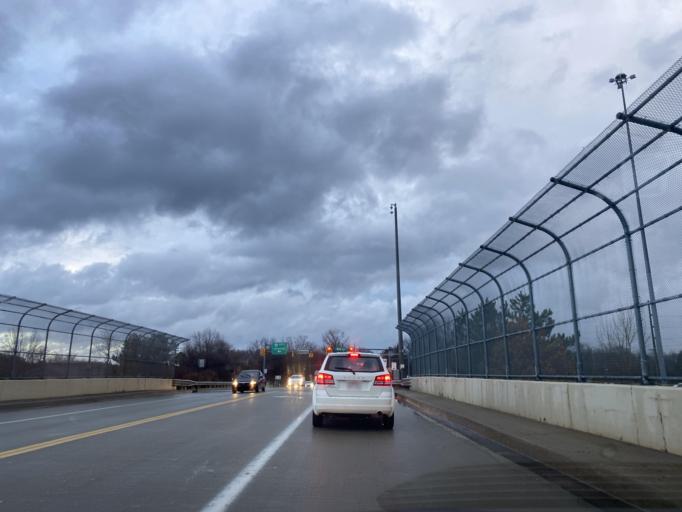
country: IN
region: Maharashtra
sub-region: Pune Division
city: Baramati
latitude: 18.1766
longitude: 74.4030
